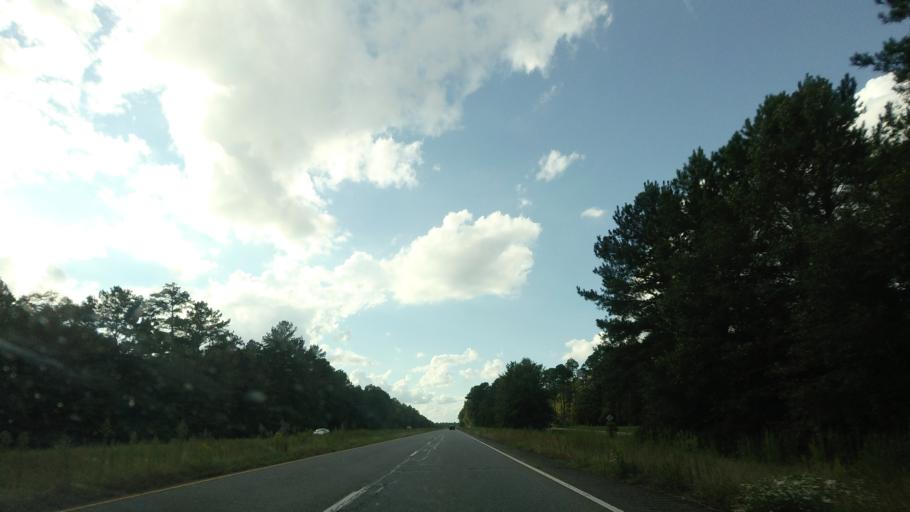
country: US
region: Georgia
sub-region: Houston County
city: Perry
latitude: 32.4200
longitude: -83.7032
